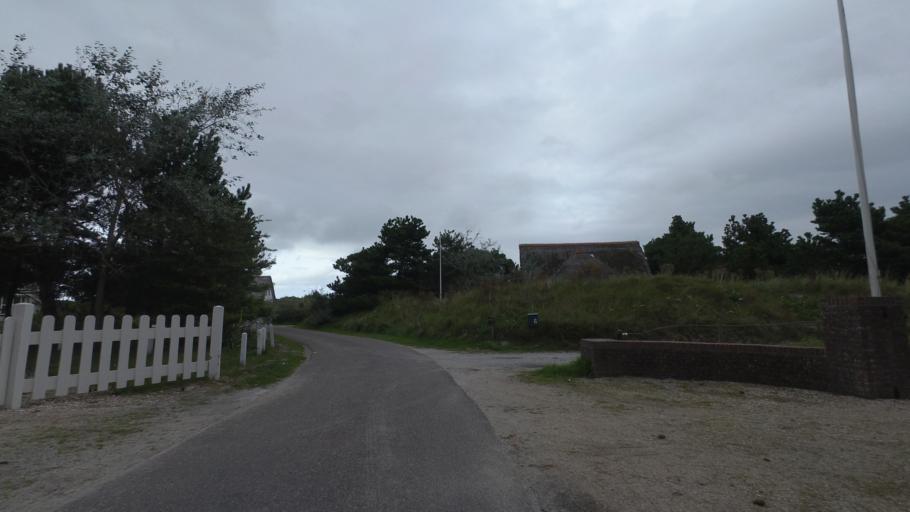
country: NL
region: Friesland
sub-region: Gemeente Ameland
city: Nes
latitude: 53.4562
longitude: 5.7945
